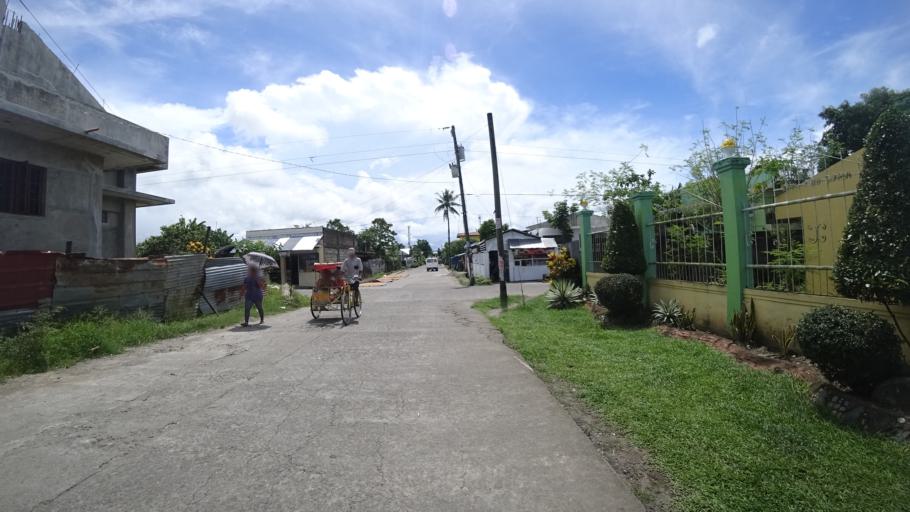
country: PH
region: Eastern Visayas
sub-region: Province of Leyte
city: Alangalang
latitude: 11.2078
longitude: 124.8462
